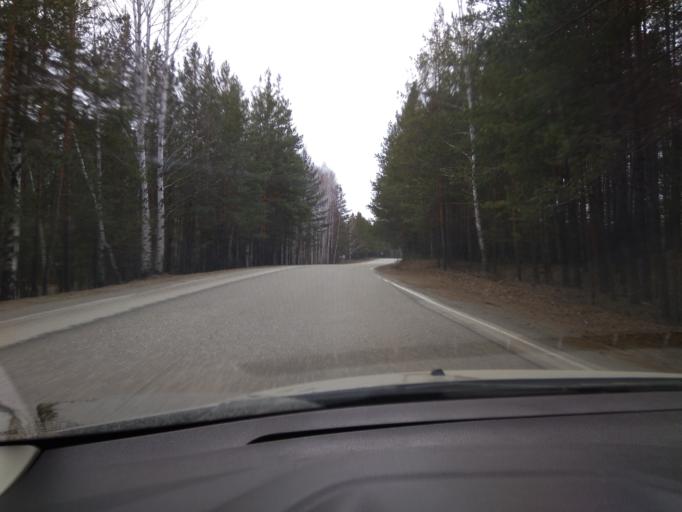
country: RU
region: Chelyabinsk
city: Kyshtym
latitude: 55.7111
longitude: 60.6032
